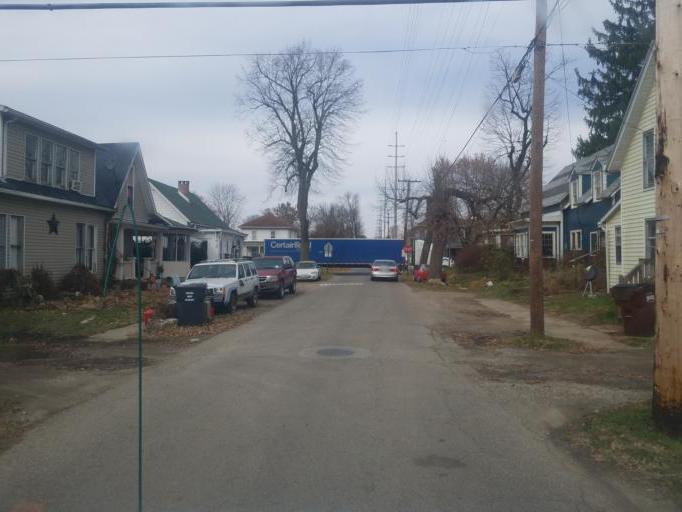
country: US
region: Ohio
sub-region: Knox County
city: Mount Vernon
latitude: 40.3936
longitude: -82.4977
